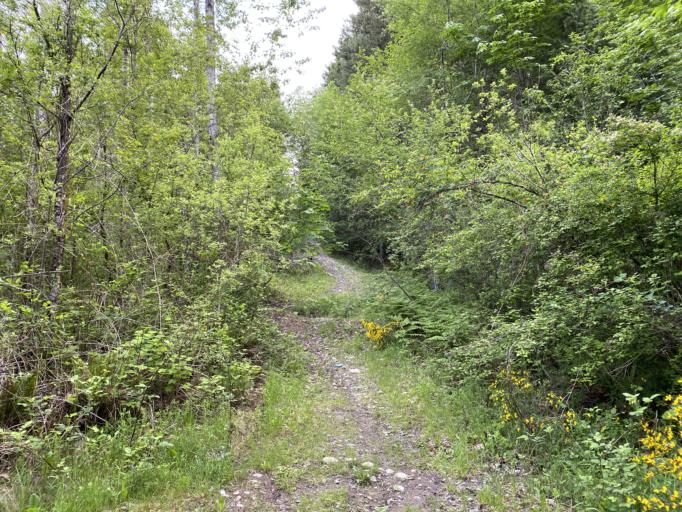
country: US
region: Washington
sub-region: Pierce County
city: Orting
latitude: 47.0856
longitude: -122.2408
